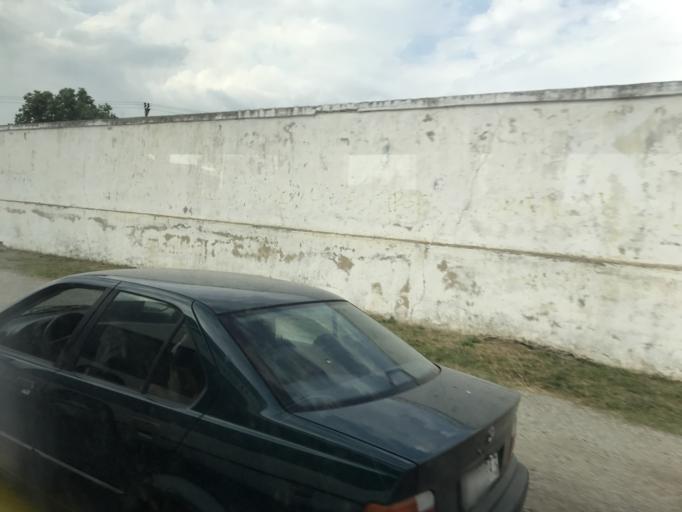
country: GR
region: East Macedonia and Thrace
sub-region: Nomos Rodopis
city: Sapes
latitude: 41.0281
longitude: 25.6865
